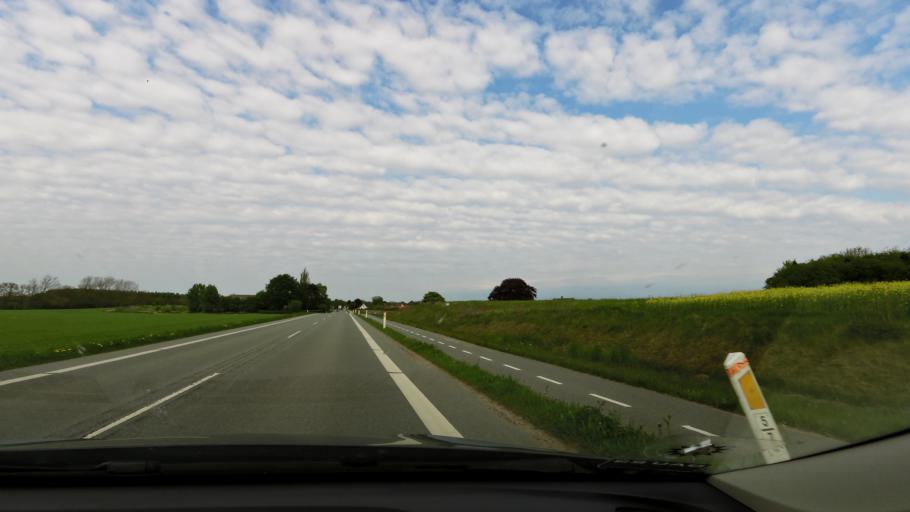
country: DK
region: South Denmark
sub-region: Nyborg Kommune
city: Nyborg
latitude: 55.3011
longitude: 10.7204
